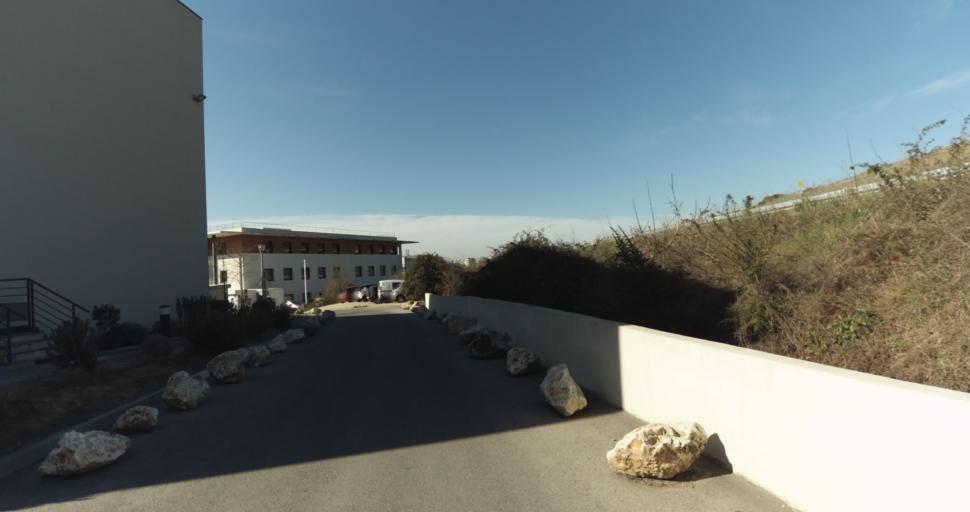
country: FR
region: Provence-Alpes-Cote d'Azur
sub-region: Departement des Bouches-du-Rhone
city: Aix-en-Provence
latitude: 43.5142
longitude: 5.4287
